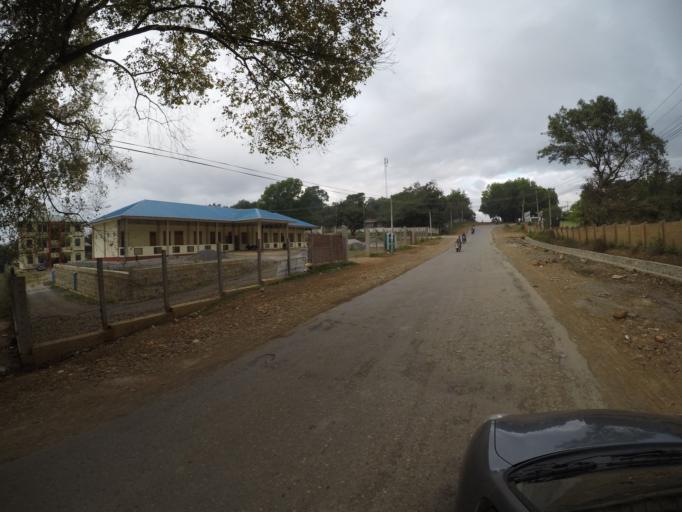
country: MM
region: Shan
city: Taunggyi
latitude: 20.7820
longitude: 96.9968
